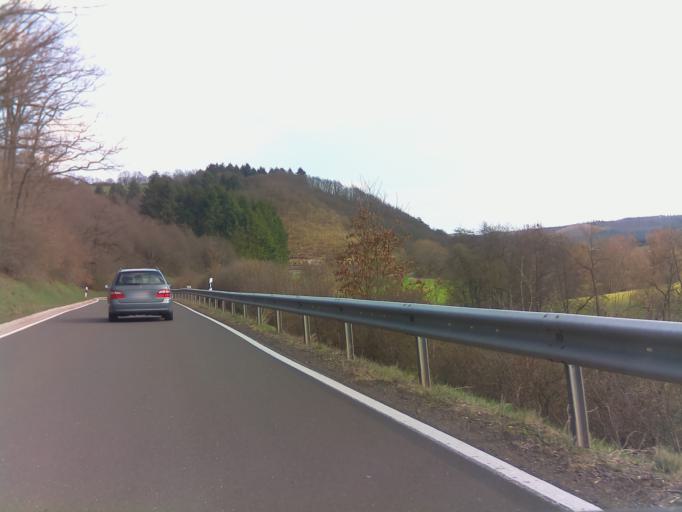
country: DE
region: Rheinland-Pfalz
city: Mittelreidenbach
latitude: 49.7406
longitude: 7.4511
